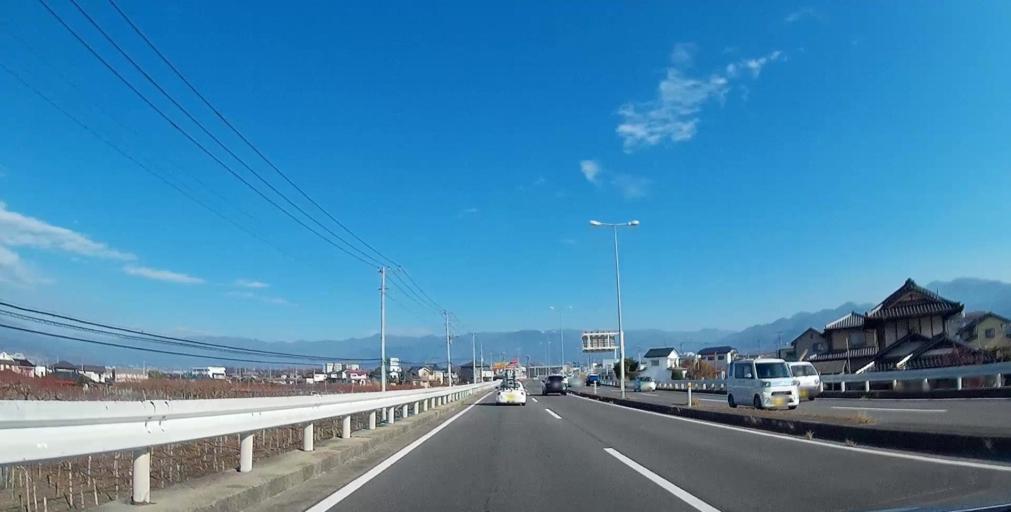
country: JP
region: Yamanashi
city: Isawa
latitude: 35.6452
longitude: 138.6538
